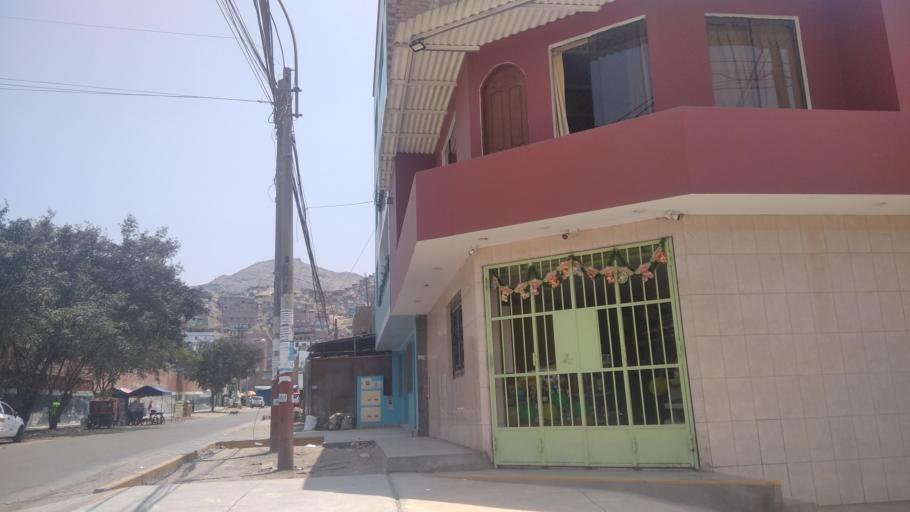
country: PE
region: Lima
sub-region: Lima
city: Independencia
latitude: -11.9675
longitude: -76.9862
